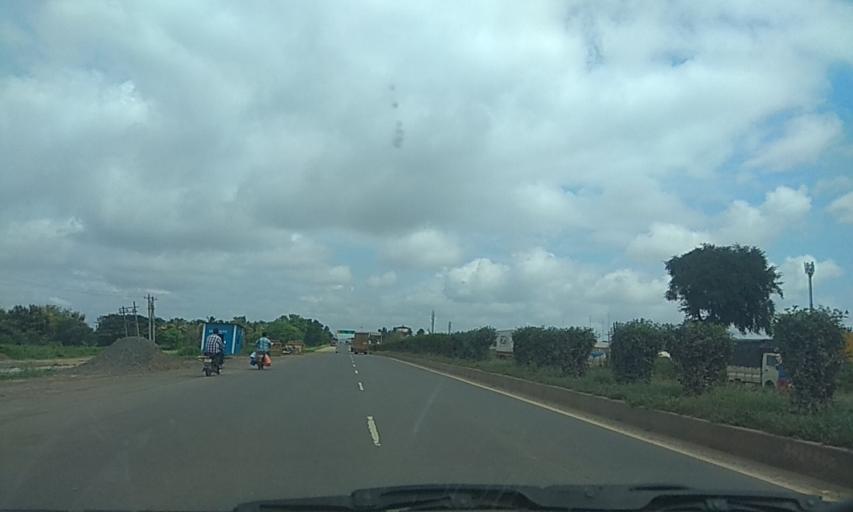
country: IN
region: Karnataka
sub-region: Dharwad
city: Hubli
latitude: 15.3100
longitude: 75.1454
